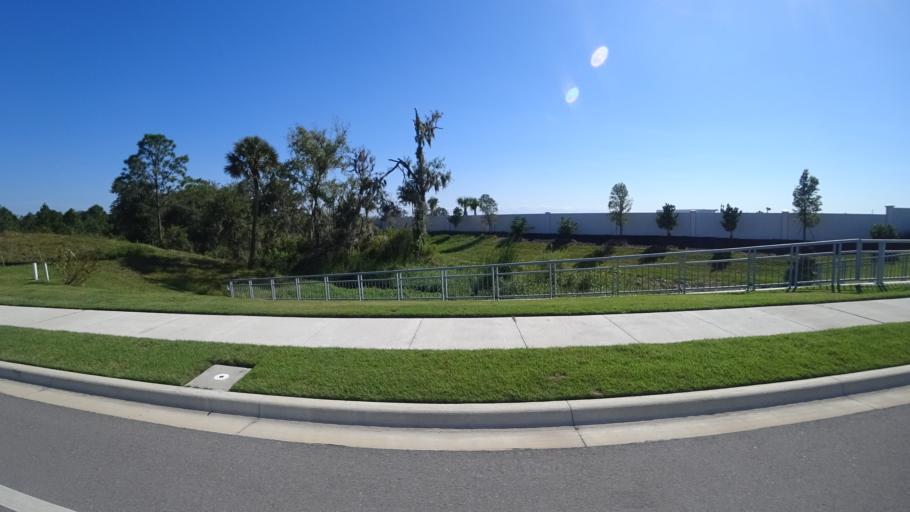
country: US
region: Florida
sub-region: Sarasota County
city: The Meadows
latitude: 27.4019
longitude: -82.3609
